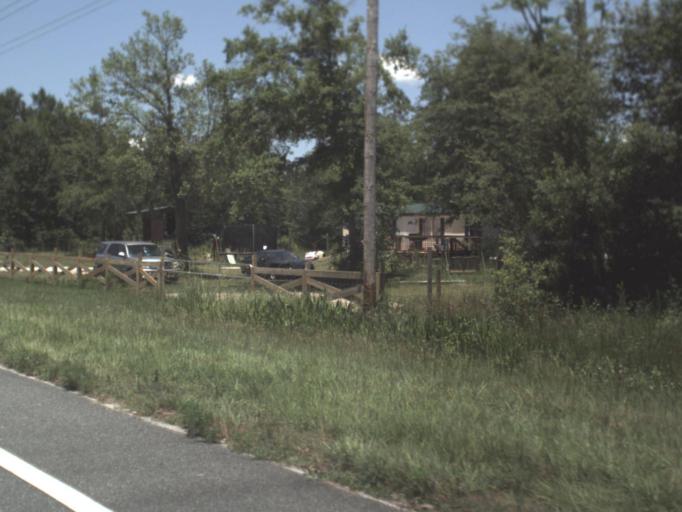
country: US
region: Florida
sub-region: Lafayette County
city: Mayo
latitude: 29.9189
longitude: -82.9511
